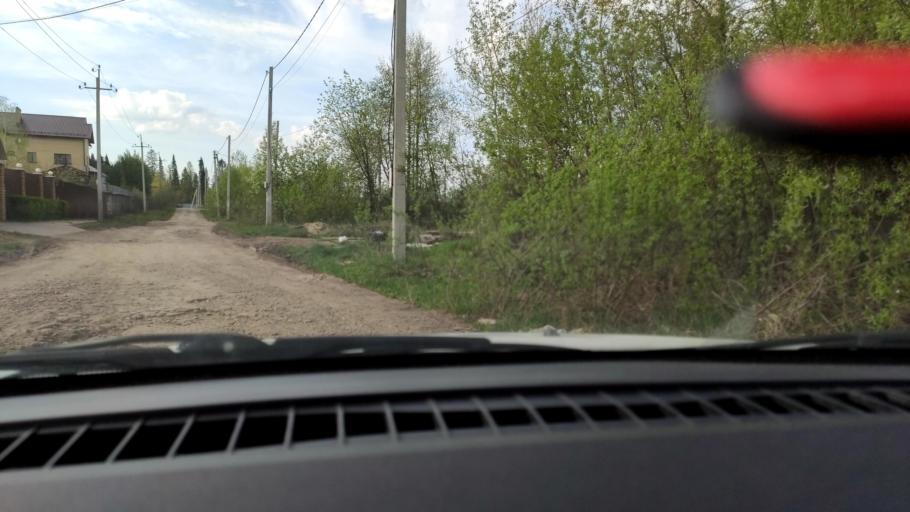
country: RU
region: Perm
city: Froly
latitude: 57.9522
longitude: 56.2849
